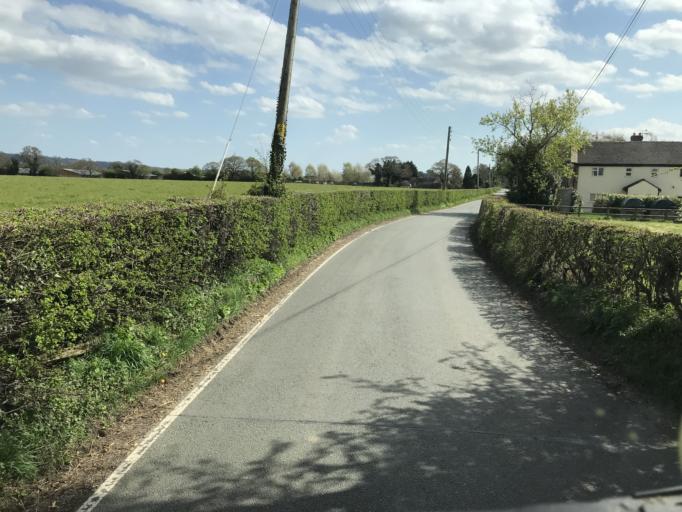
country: GB
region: England
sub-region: Cheshire West and Chester
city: Tarvin
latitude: 53.2103
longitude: -2.7691
